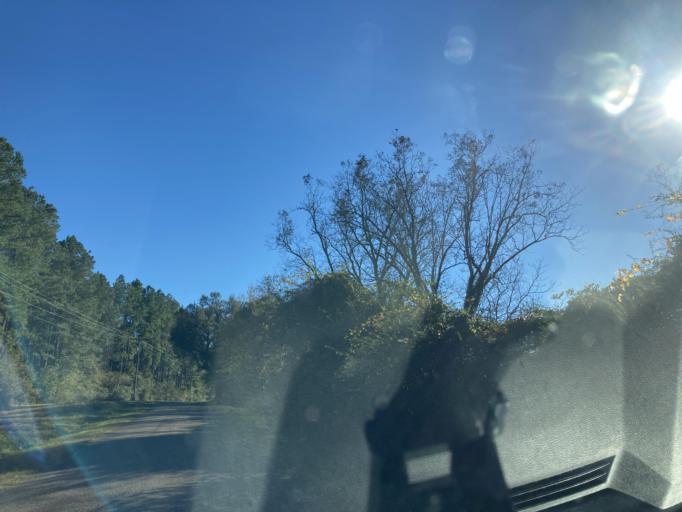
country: US
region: Mississippi
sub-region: Lamar County
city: Sumrall
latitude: 31.3573
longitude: -89.6033
